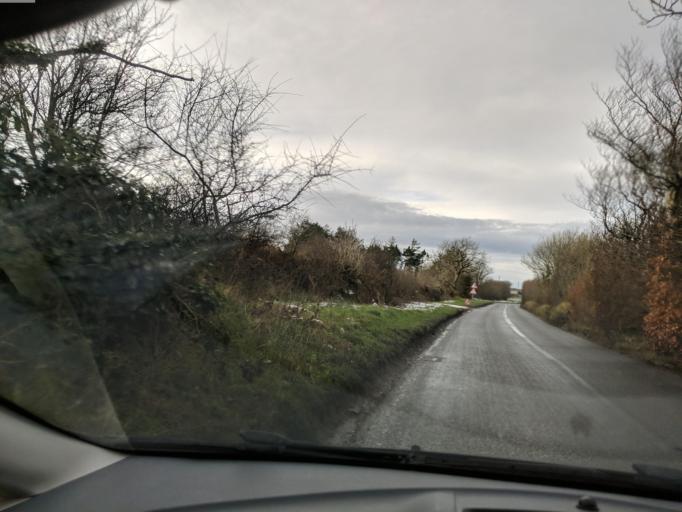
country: GB
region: England
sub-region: Cornwall
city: Jacobstow
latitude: 50.6733
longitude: -4.6075
